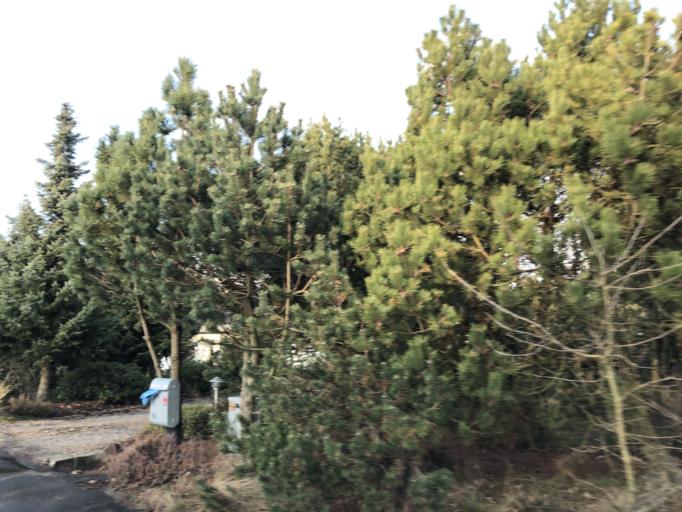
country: DK
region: Central Jutland
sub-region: Holstebro Kommune
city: Ulfborg
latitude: 56.3205
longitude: 8.4354
